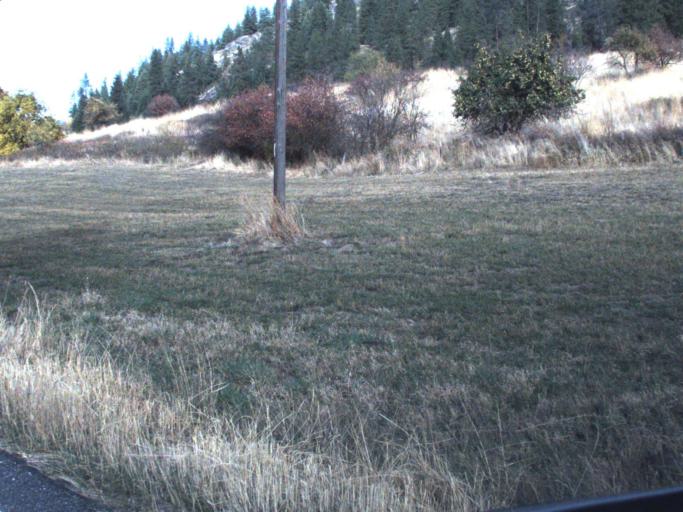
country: US
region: Washington
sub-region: Stevens County
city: Kettle Falls
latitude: 48.3995
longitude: -118.1684
